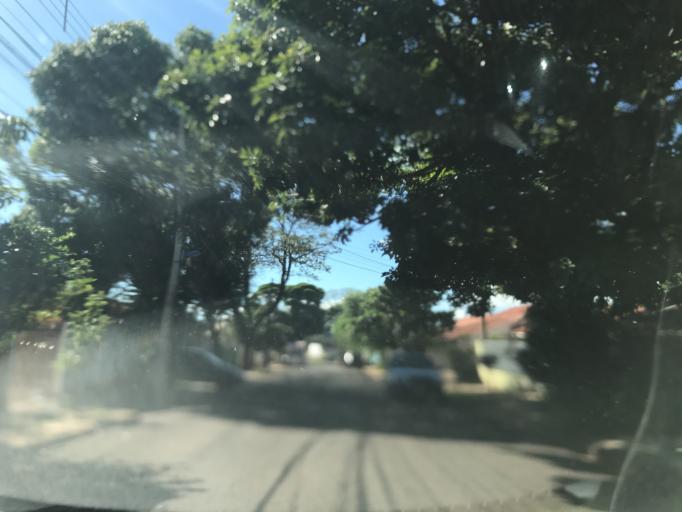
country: BR
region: Parana
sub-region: Maringa
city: Maringa
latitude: -23.4518
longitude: -51.9556
